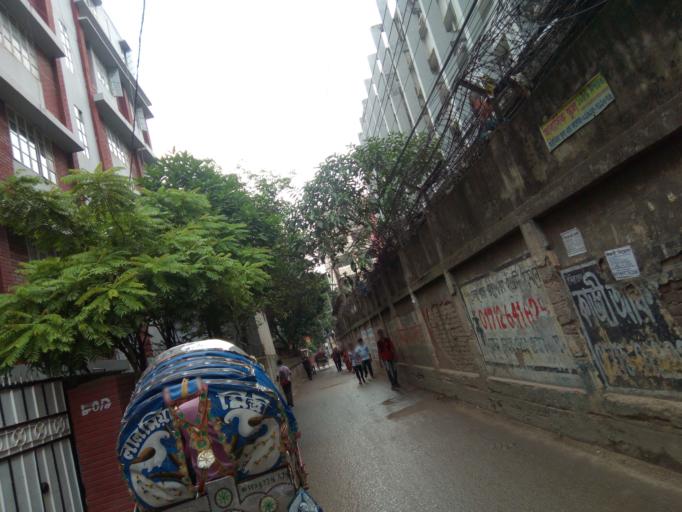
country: BD
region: Dhaka
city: Azimpur
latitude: 23.7580
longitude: 90.3824
